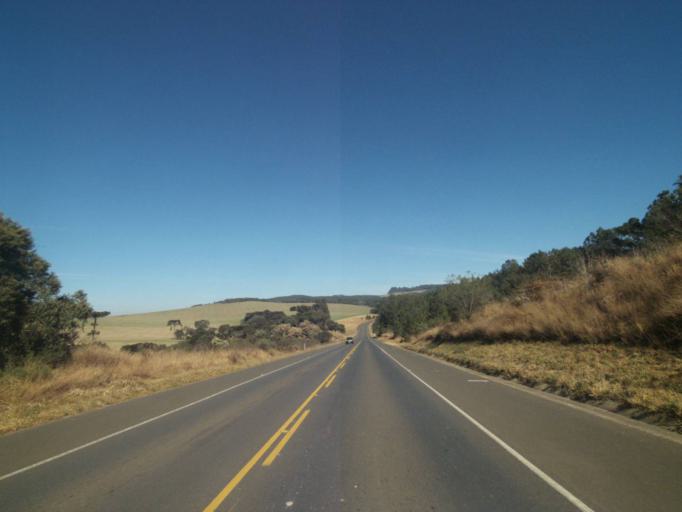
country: BR
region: Parana
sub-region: Tibagi
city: Tibagi
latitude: -24.5452
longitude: -50.4502
